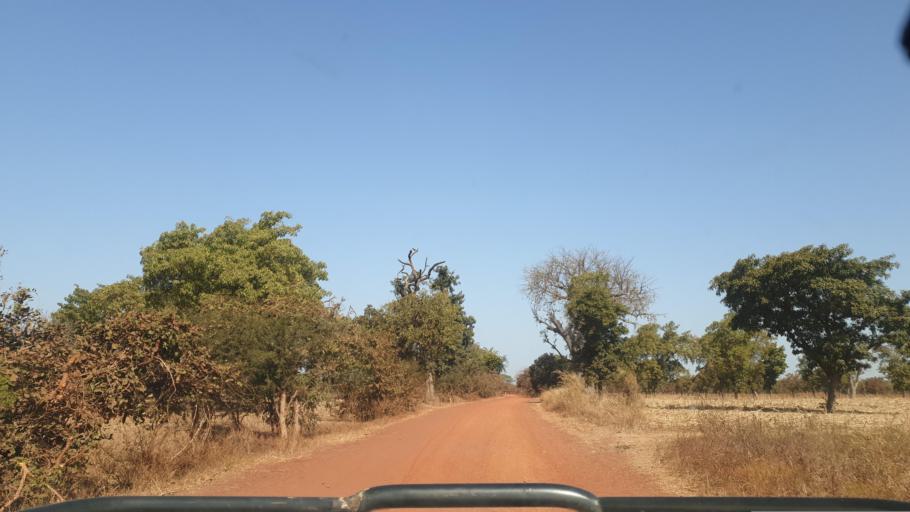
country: ML
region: Sikasso
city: Bougouni
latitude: 11.8439
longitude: -6.9783
